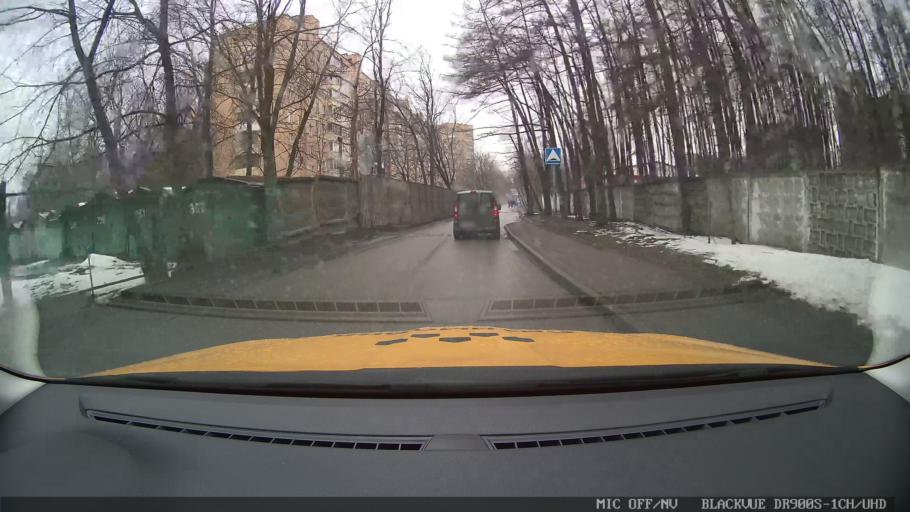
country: RU
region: Moscow
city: Vatutino
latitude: 55.8612
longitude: 37.7003
